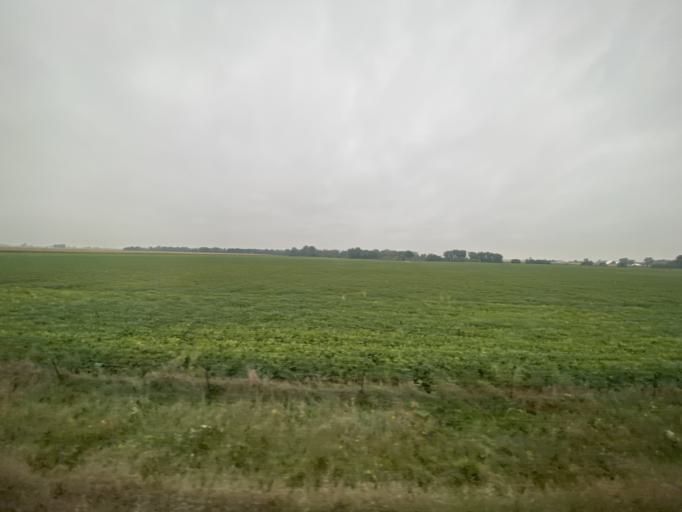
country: US
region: Illinois
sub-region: DeKalb County
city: Somonauk
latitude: 41.6198
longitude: -88.7633
